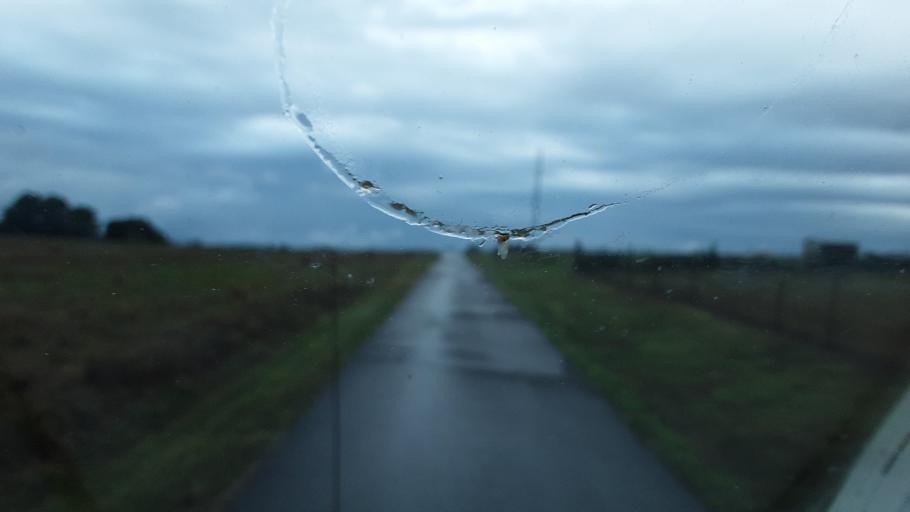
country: US
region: North Carolina
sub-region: Yadkin County
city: Jonesville
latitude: 36.0812
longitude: -80.8742
